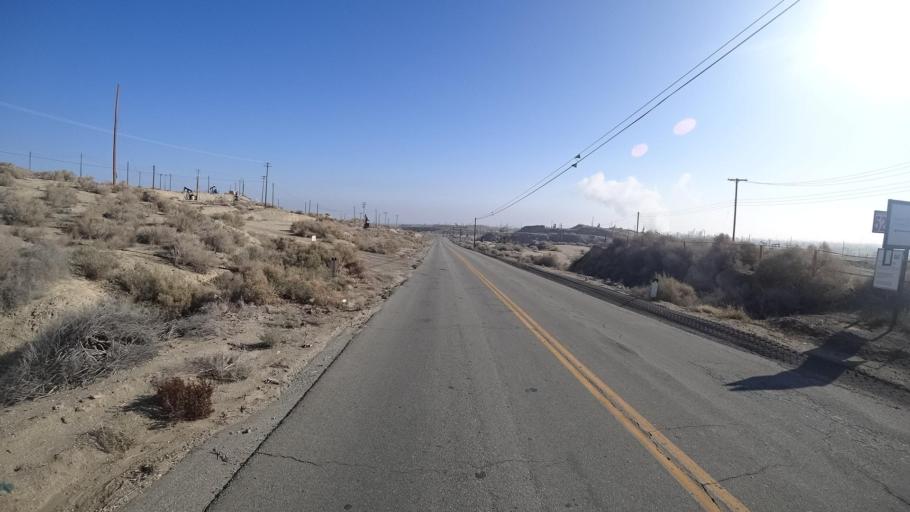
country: US
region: California
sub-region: Kern County
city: Taft Heights
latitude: 35.2194
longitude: -119.6038
